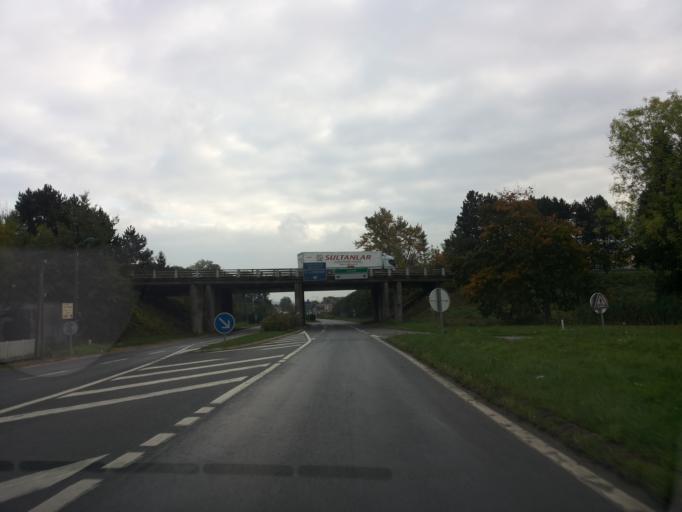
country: FR
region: Champagne-Ardenne
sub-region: Departement des Ardennes
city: Donchery
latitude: 49.6941
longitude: 4.9040
